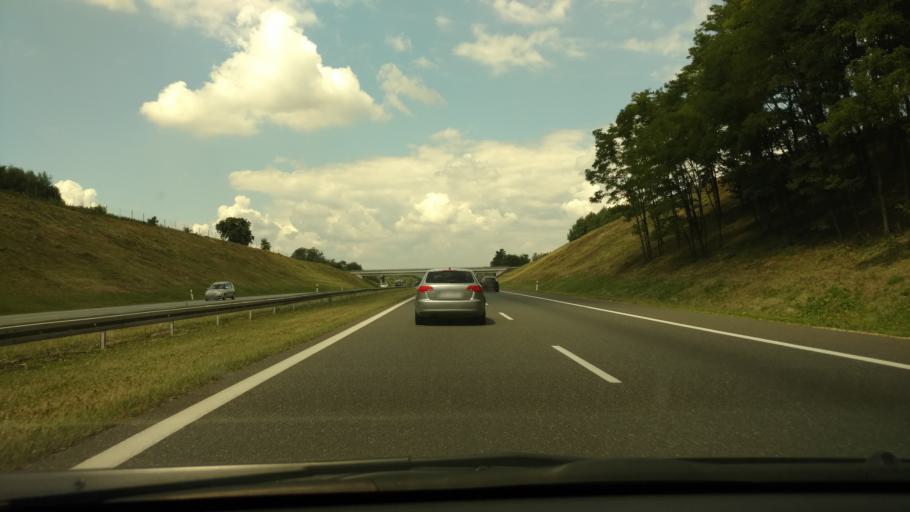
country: PL
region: Lesser Poland Voivodeship
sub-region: Powiat krakowski
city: Czulow
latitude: 50.0834
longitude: 19.7017
